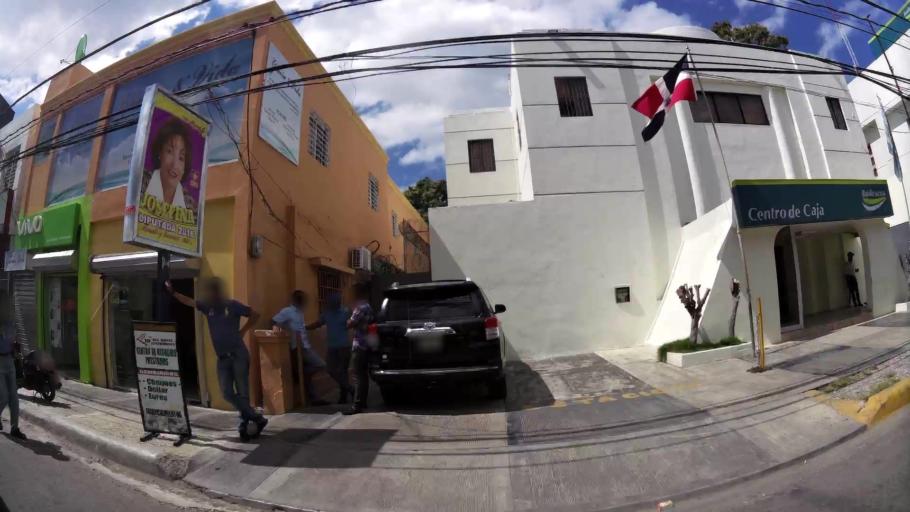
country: DO
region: San Cristobal
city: San Cristobal
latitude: 18.4168
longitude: -70.1112
